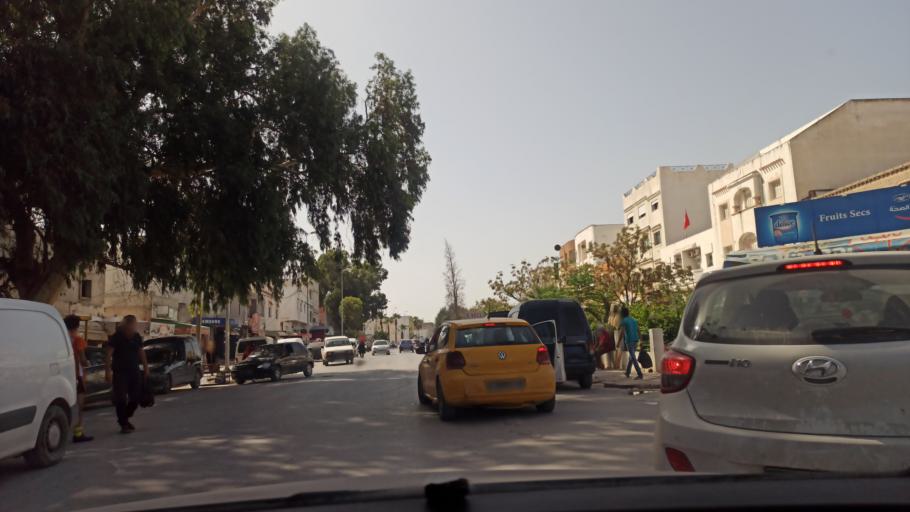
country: TN
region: Manouba
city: Manouba
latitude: 36.7666
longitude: 10.1112
